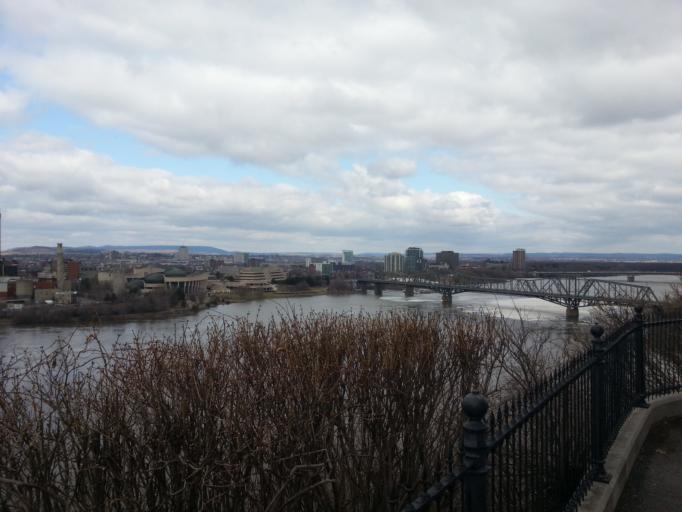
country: CA
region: Ontario
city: Ottawa
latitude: 45.4252
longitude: -75.7014
